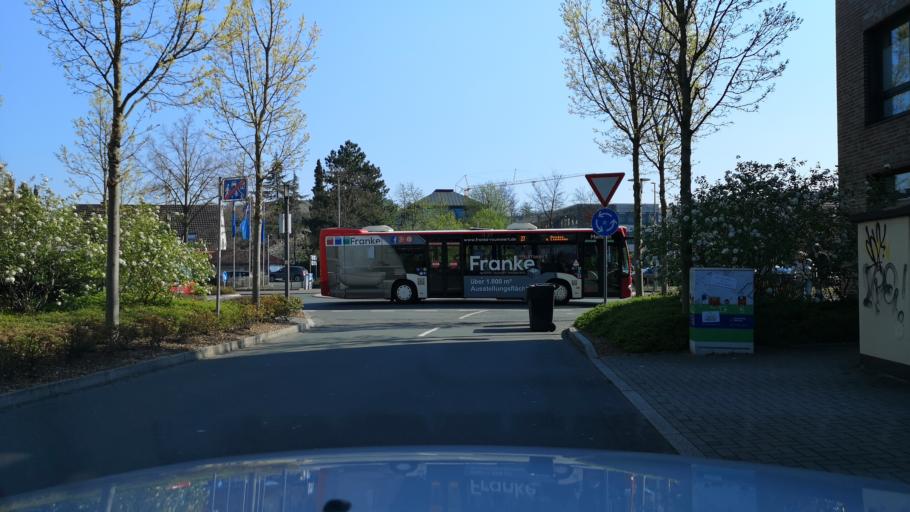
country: DE
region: North Rhine-Westphalia
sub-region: Regierungsbezirk Arnsberg
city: Menden
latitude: 51.4383
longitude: 7.7894
